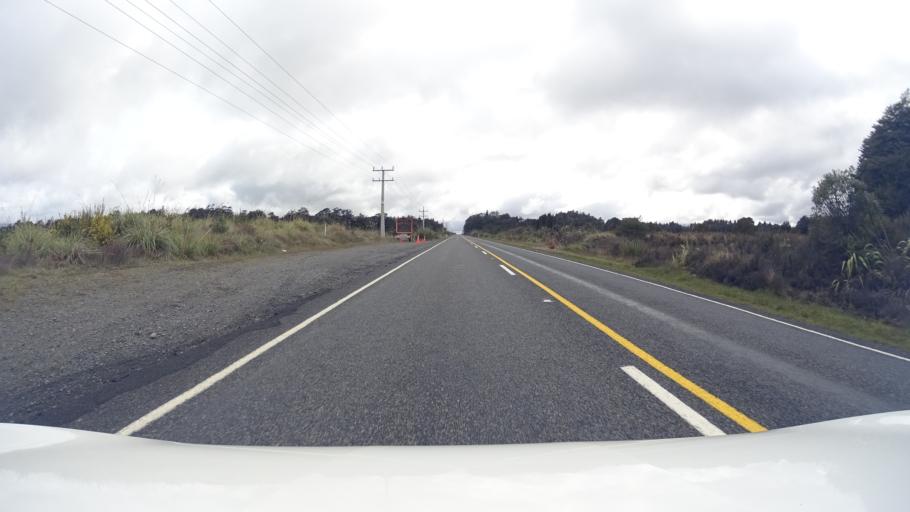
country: NZ
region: Manawatu-Wanganui
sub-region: Ruapehu District
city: Waiouru
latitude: -39.1733
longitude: 175.4750
